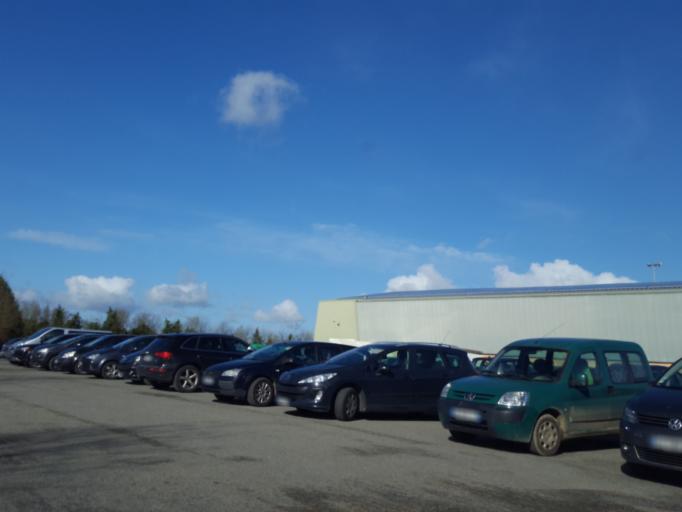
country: FR
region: Brittany
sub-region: Departement d'Ille-et-Vilaine
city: Chavagne
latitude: 48.0535
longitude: -1.7938
